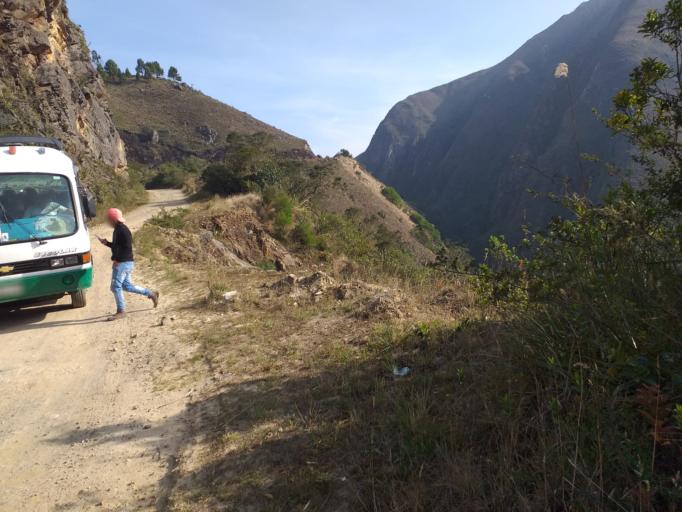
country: CO
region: Boyaca
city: Aquitania
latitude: 5.4575
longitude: -72.9217
